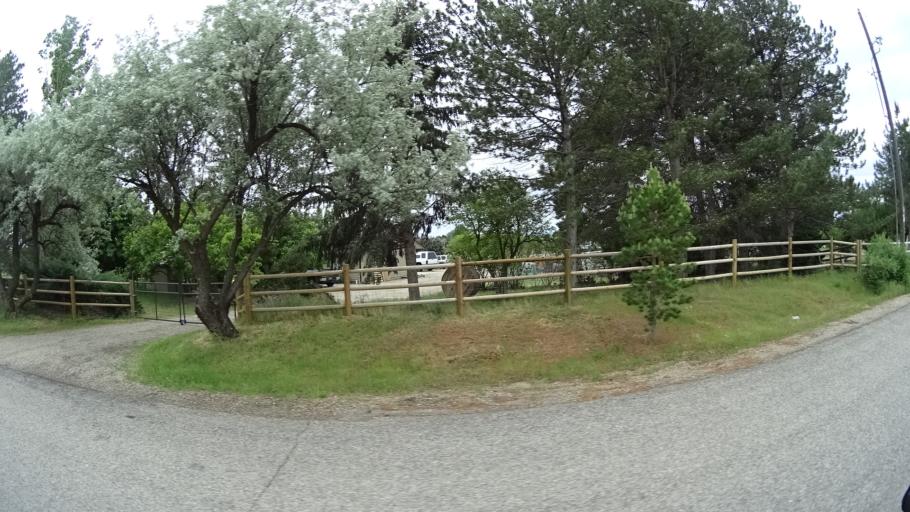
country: US
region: Idaho
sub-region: Ada County
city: Eagle
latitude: 43.7353
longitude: -116.3892
